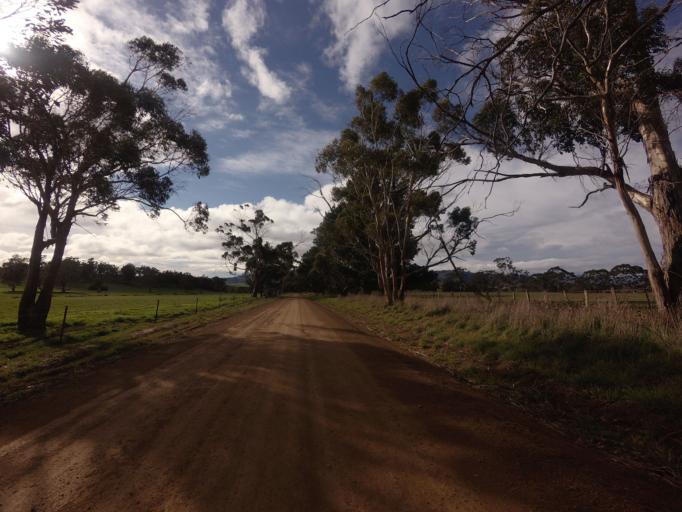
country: AU
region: Tasmania
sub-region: Derwent Valley
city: New Norfolk
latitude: -42.7145
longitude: 146.8856
